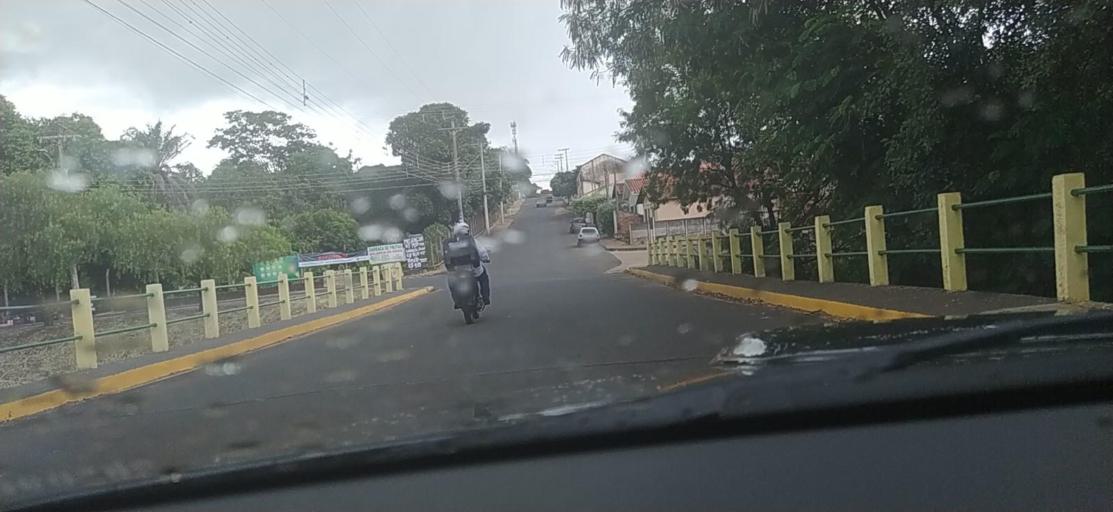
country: BR
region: Sao Paulo
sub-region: Pindorama
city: Pindorama
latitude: -21.1850
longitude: -48.9031
